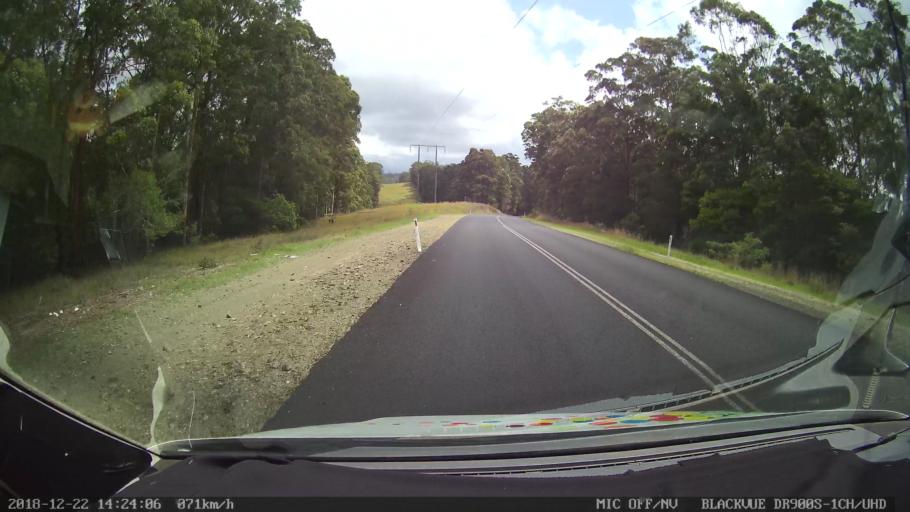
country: AU
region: New South Wales
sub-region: Bellingen
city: Dorrigo
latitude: -30.0407
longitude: 152.6473
